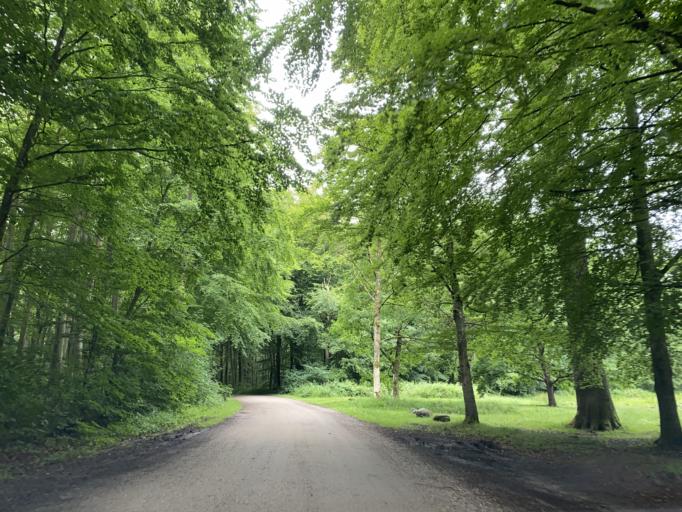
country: DK
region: South Denmark
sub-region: Sonderborg Kommune
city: Sonderborg
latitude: 54.9028
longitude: 9.8353
